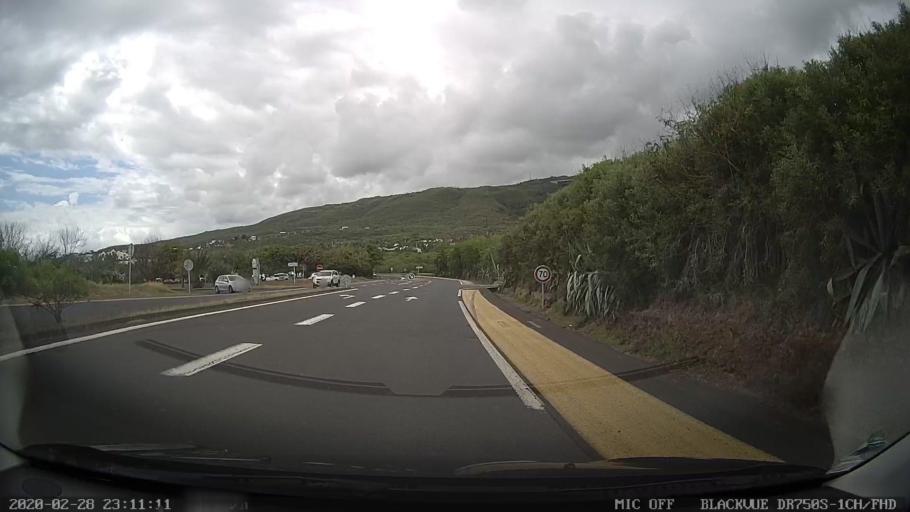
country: RE
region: Reunion
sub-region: Reunion
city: Trois-Bassins
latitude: -21.1120
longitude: 55.2558
